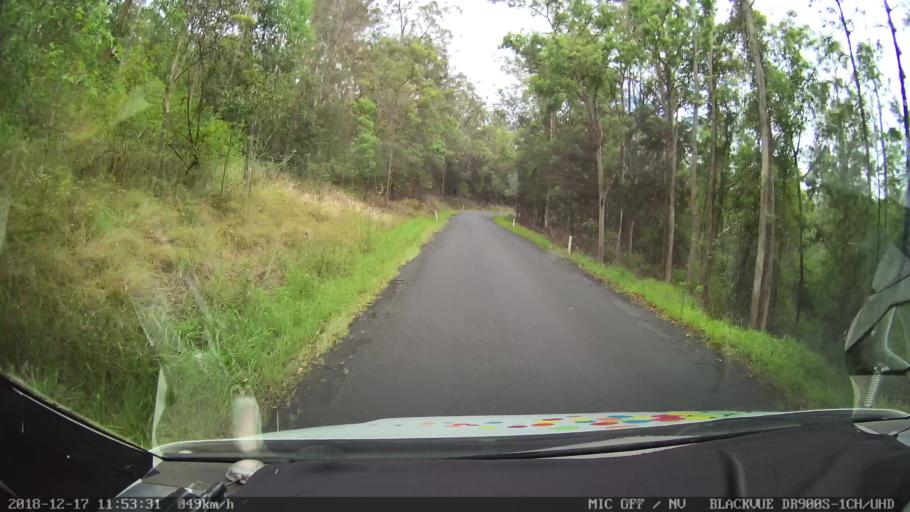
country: AU
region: New South Wales
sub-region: Kyogle
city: Kyogle
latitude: -28.5734
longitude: 152.5861
